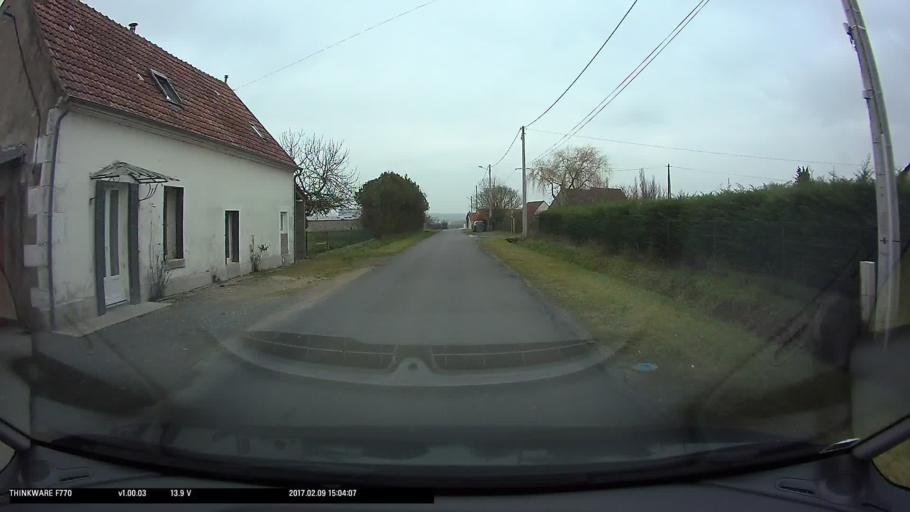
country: FR
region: Centre
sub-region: Departement du Cher
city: Orval
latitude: 46.8050
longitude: 2.4618
